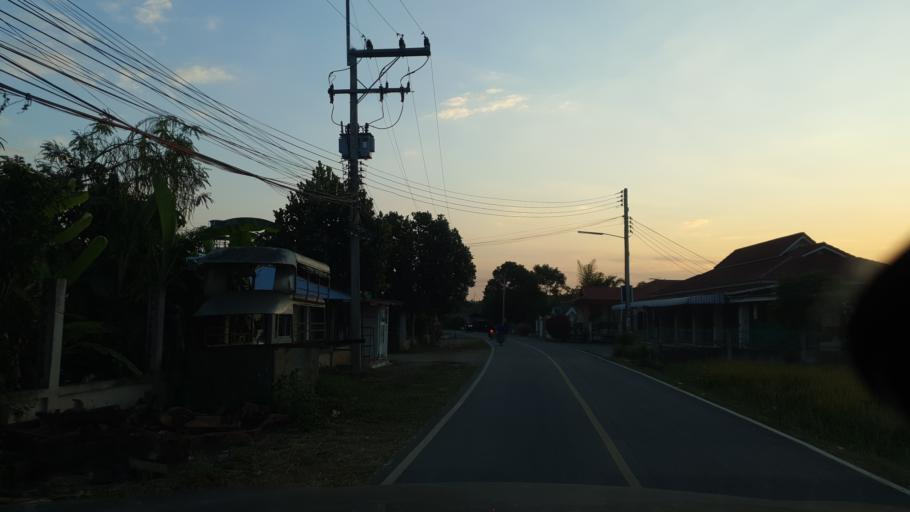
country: TH
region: Chiang Mai
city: San Sai
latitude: 18.8504
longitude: 99.0726
